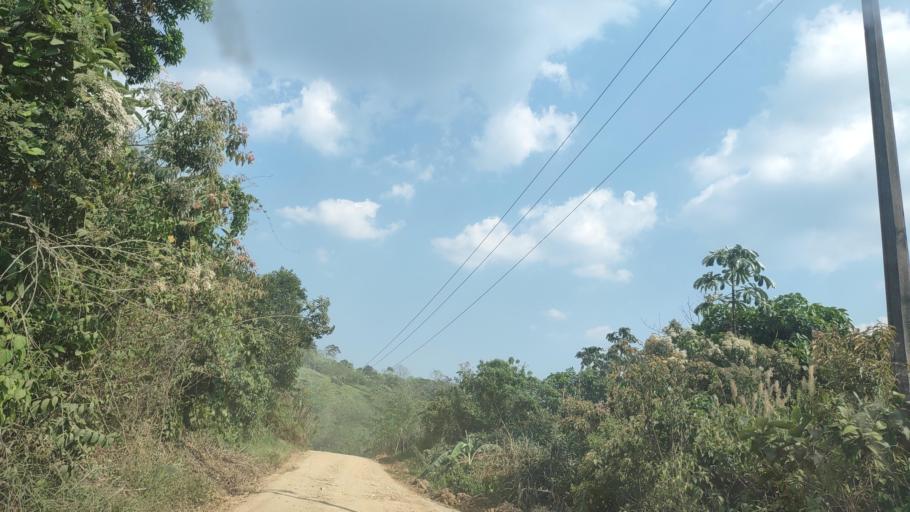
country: MX
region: Chiapas
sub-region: Tecpatan
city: Raudales Malpaso
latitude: 17.3305
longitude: -93.7478
